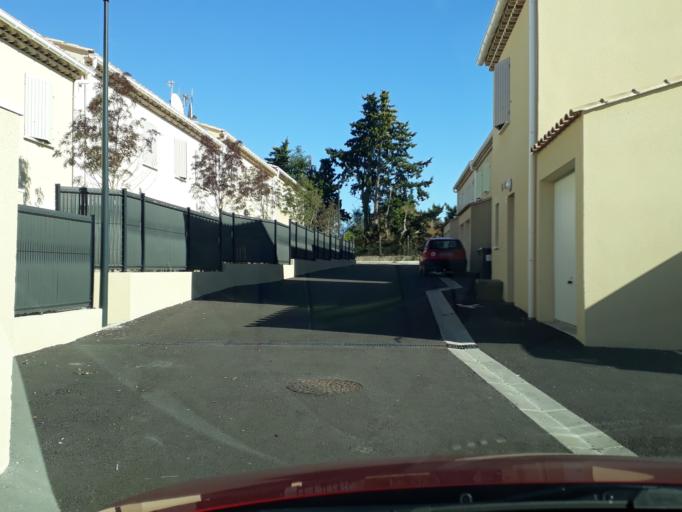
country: FR
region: Provence-Alpes-Cote d'Azur
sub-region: Departement du Vaucluse
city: Carpentras
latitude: 44.0582
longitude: 5.0707
